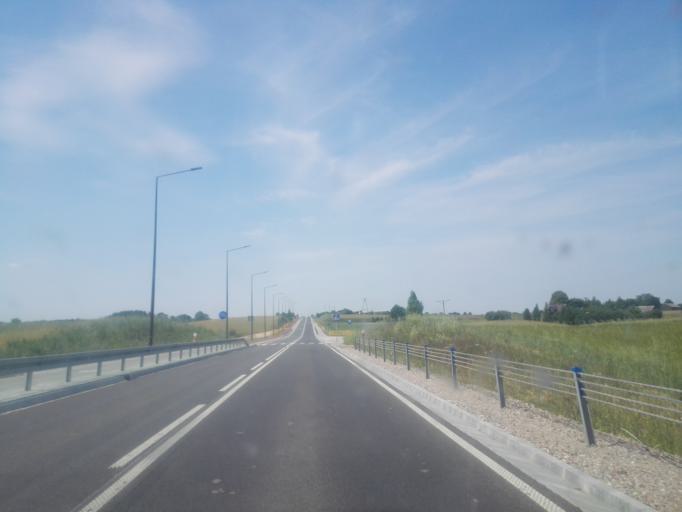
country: PL
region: Podlasie
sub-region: Powiat sejnenski
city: Sejny
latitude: 54.1099
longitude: 23.3114
